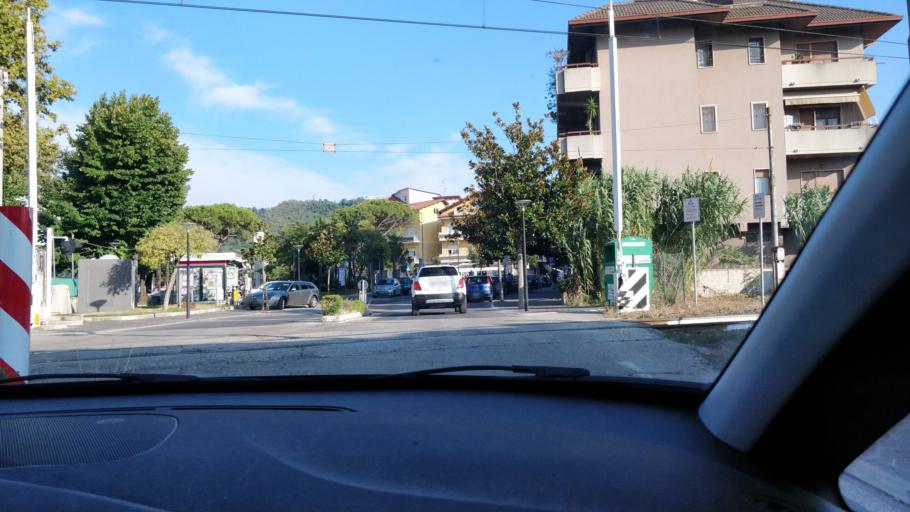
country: IT
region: Abruzzo
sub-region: Provincia di Chieti
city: Sambuceto
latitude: 42.4238
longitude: 14.1864
